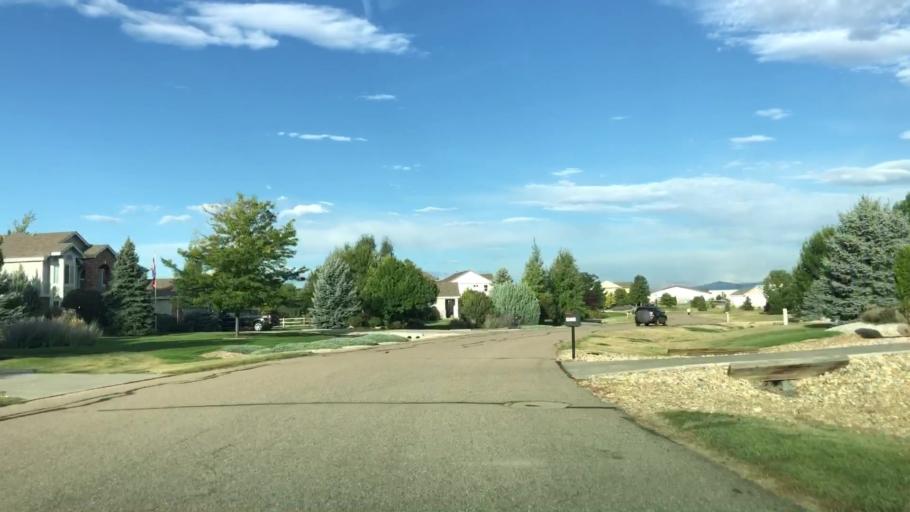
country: US
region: Colorado
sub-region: Weld County
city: Windsor
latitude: 40.4376
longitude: -104.9589
